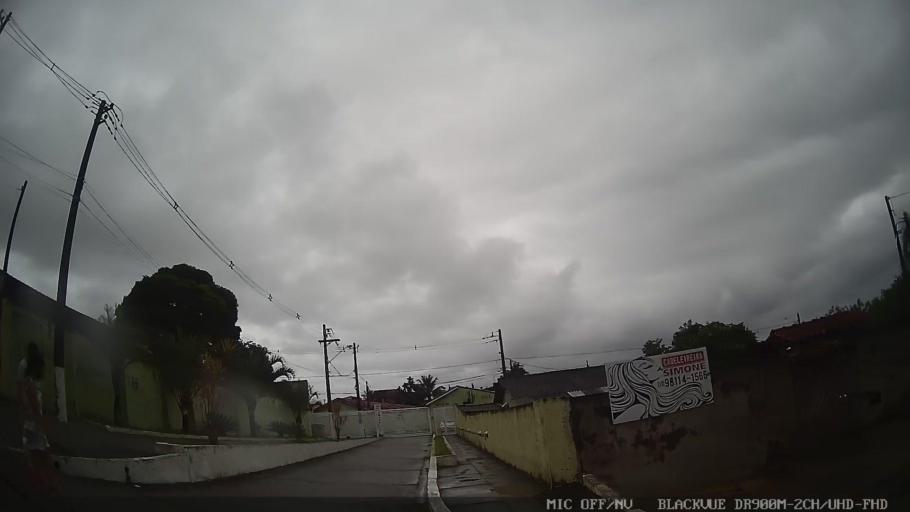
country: BR
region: Sao Paulo
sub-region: Itanhaem
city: Itanhaem
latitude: -24.1797
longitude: -46.8203
